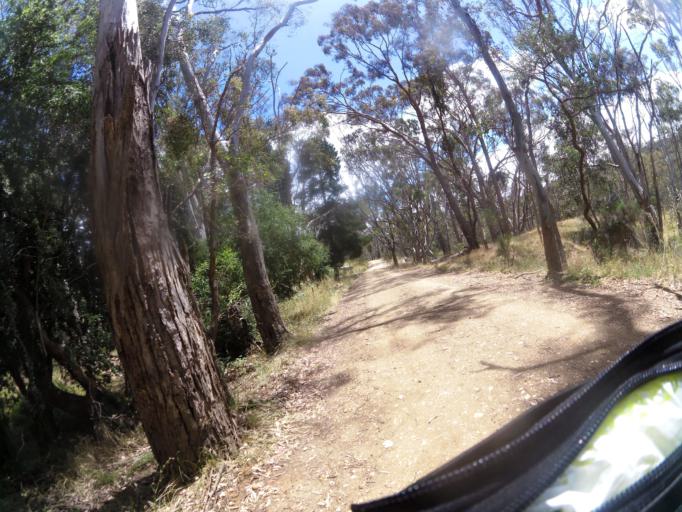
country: AU
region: Victoria
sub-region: Mount Alexander
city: Castlemaine
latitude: -37.0583
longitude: 144.2719
